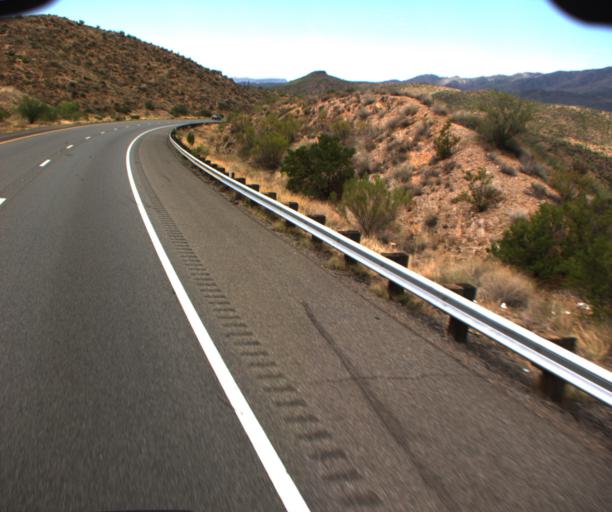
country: US
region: Arizona
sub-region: Yavapai County
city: Black Canyon City
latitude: 34.1551
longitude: -112.1463
